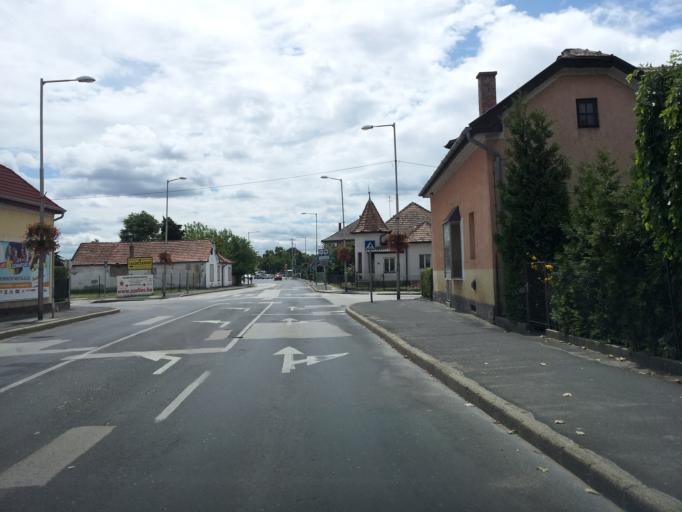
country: HU
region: Somogy
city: Siofok
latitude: 46.9039
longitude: 18.0466
